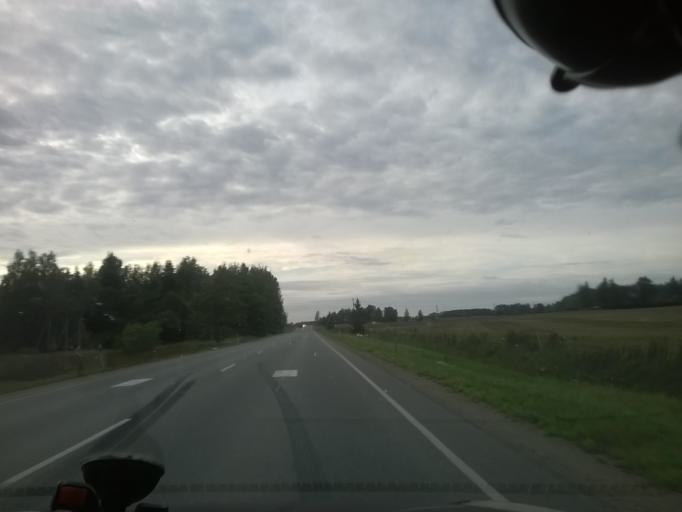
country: EE
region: Vorumaa
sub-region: Voru linn
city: Voru
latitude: 57.8754
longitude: 26.8998
